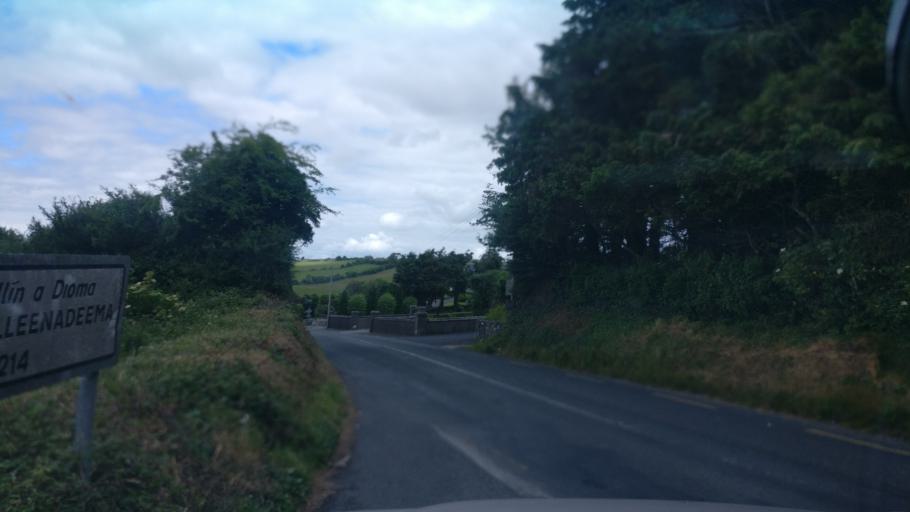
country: IE
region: Connaught
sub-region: County Galway
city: Loughrea
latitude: 53.1811
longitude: -8.5551
